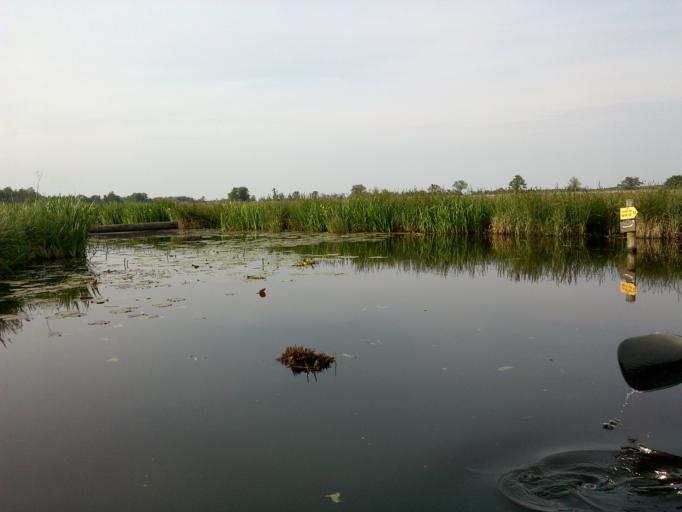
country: NL
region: South Holland
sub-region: Gemeente Nieuwkoop
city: Nieuwkoop
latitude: 52.1376
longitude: 4.7943
